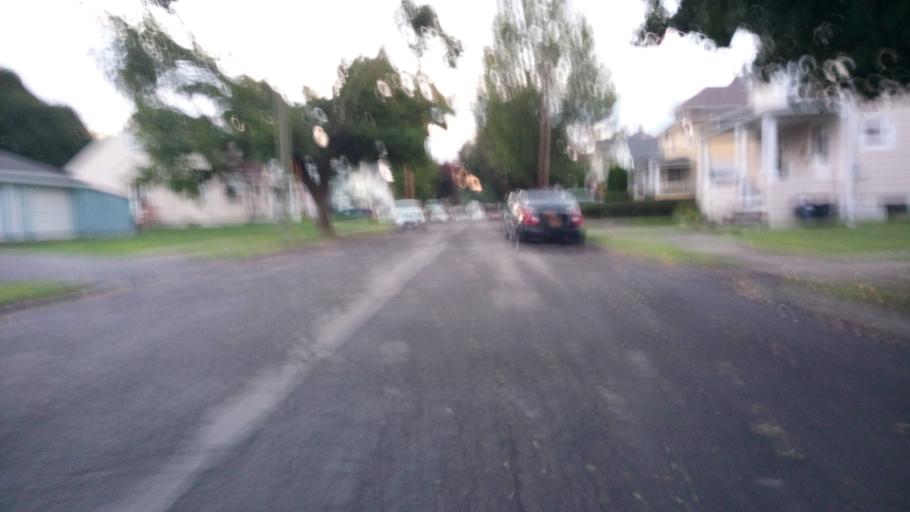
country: US
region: New York
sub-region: Chemung County
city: Elmira
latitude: 42.1006
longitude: -76.8222
